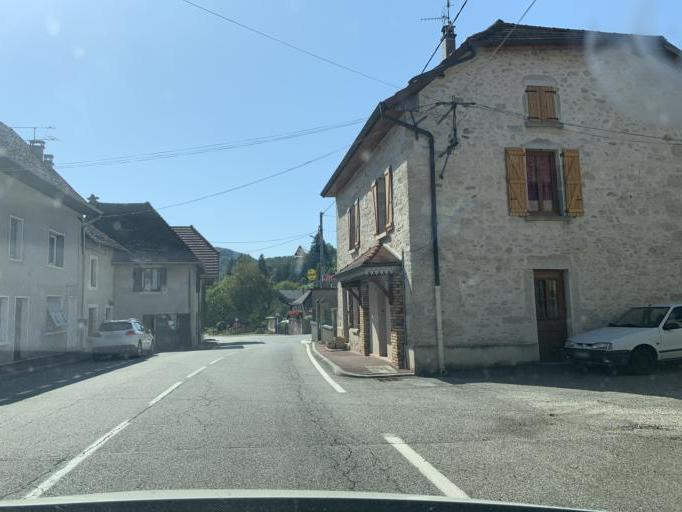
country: FR
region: Rhone-Alpes
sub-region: Departement de la Savoie
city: Yenne
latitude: 45.6788
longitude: 5.6761
